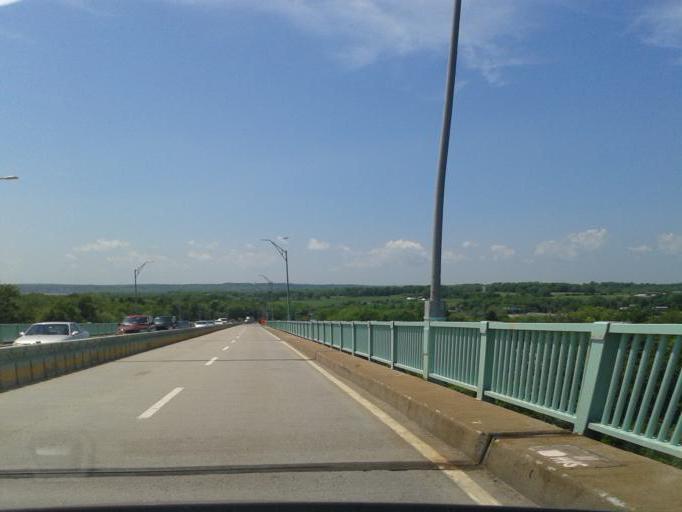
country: US
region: Rhode Island
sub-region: Newport County
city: Jamestown
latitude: 41.5075
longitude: -71.3594
